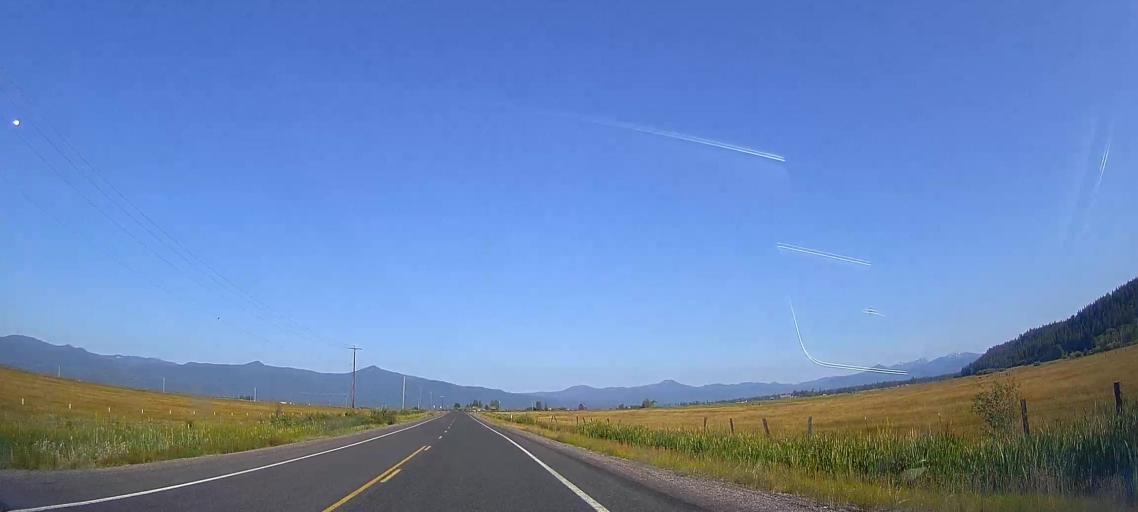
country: US
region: Oregon
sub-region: Klamath County
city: Klamath Falls
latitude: 42.6448
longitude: -121.9479
